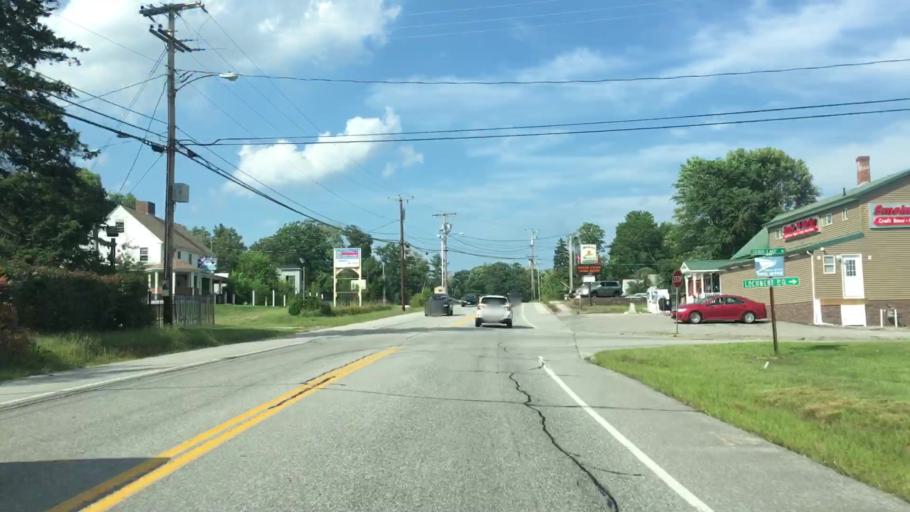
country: US
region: New Hampshire
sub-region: Belknap County
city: Sanbornton
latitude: 43.4753
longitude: -71.5432
